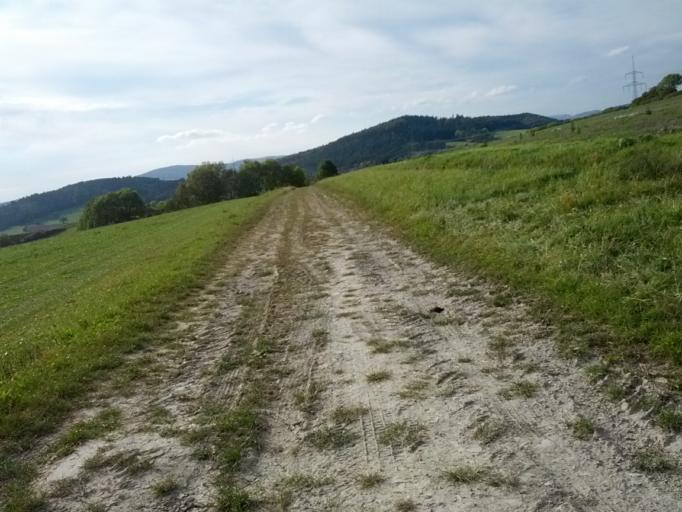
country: DE
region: Thuringia
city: Krauthausen
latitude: 51.0257
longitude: 10.3109
